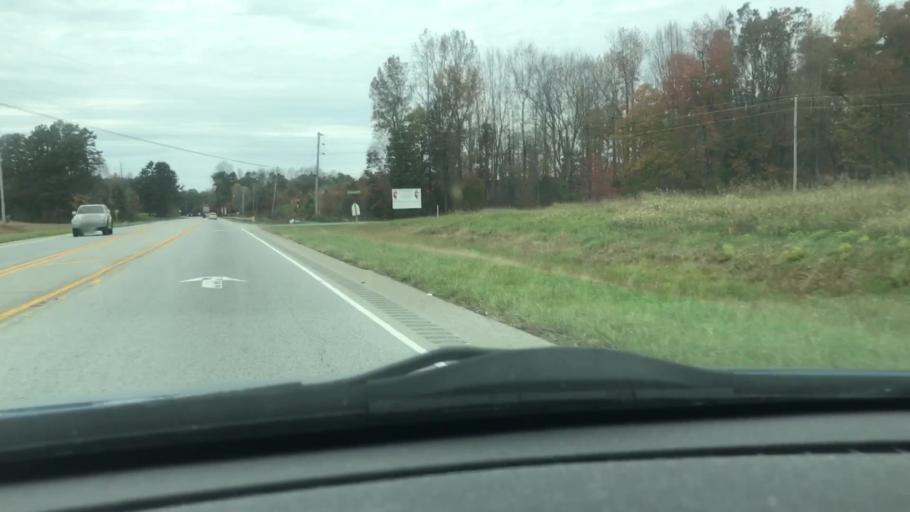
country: US
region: North Carolina
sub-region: Randolph County
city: Trinity
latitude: 35.7473
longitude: -80.0064
